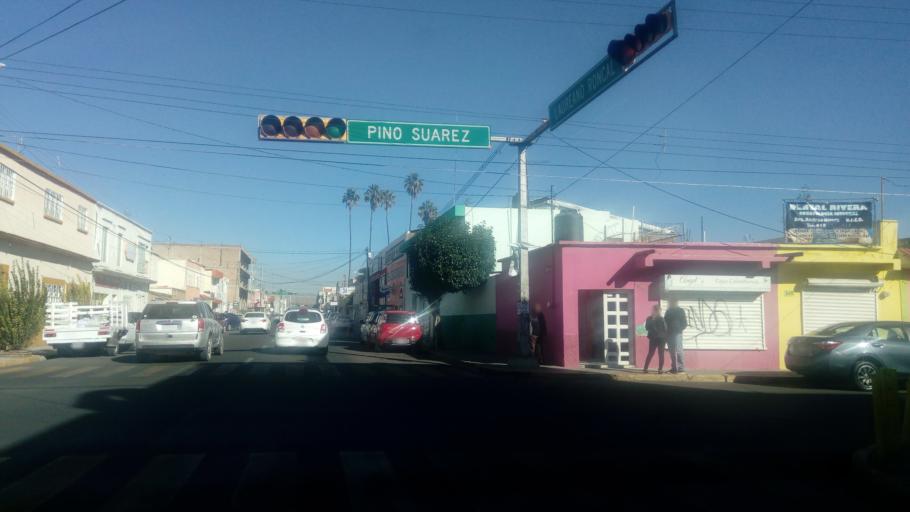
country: MX
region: Durango
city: Victoria de Durango
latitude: 24.0241
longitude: -104.6574
